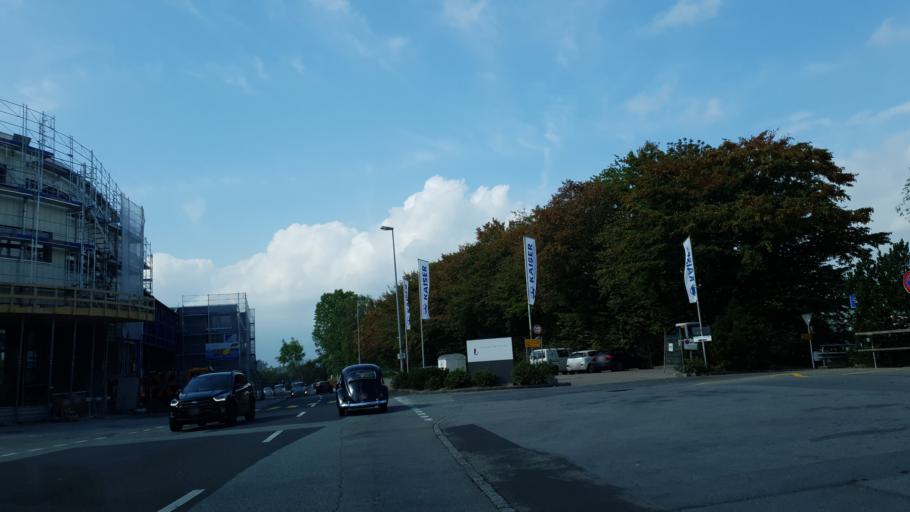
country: LI
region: Mauren
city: Mauren
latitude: 47.2176
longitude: 9.5689
